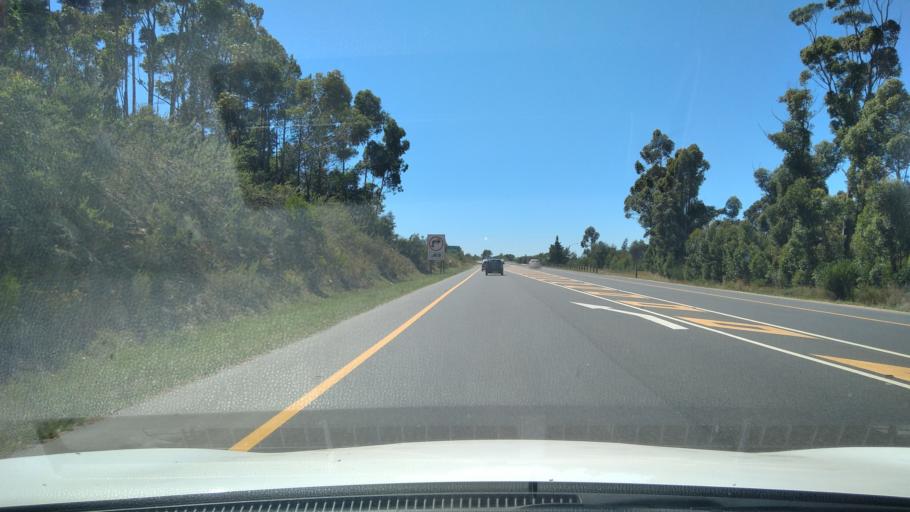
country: ZA
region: Western Cape
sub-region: Overberg District Municipality
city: Caledon
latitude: -34.2241
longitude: 19.4132
